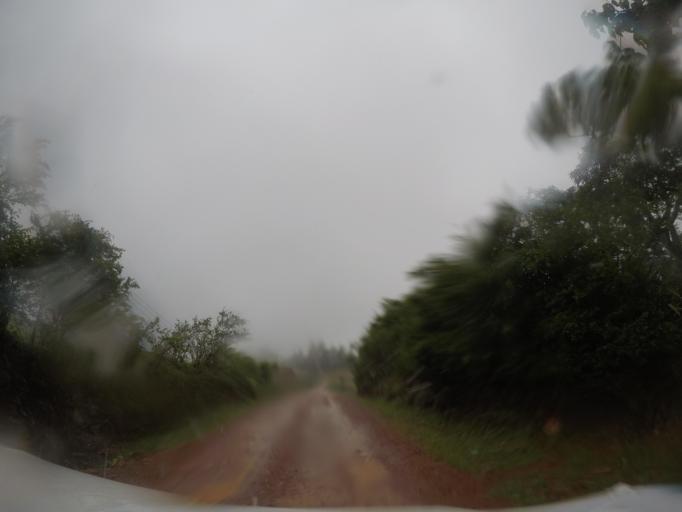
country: TL
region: Baucau
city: Venilale
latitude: -8.6374
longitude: 126.4098
